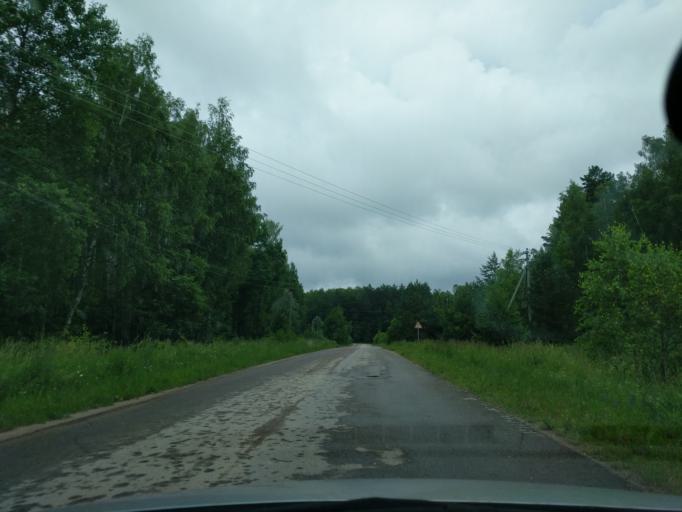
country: RU
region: Kaluga
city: Myatlevo
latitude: 54.8271
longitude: 35.6675
